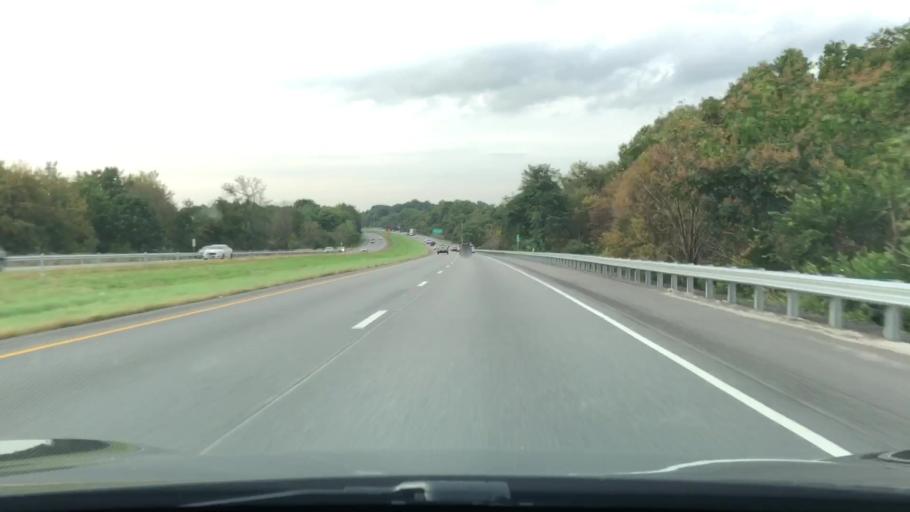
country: US
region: Pennsylvania
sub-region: Bucks County
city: Woodside
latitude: 40.2058
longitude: -74.8749
